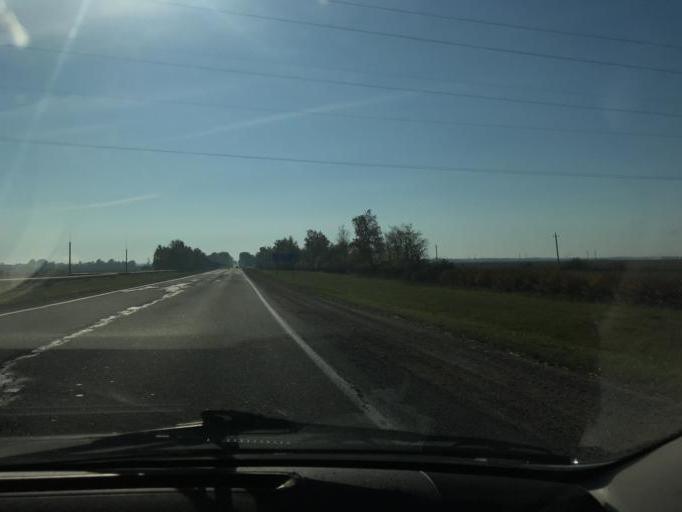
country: BY
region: Minsk
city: Salihorsk
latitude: 52.8487
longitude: 27.4663
